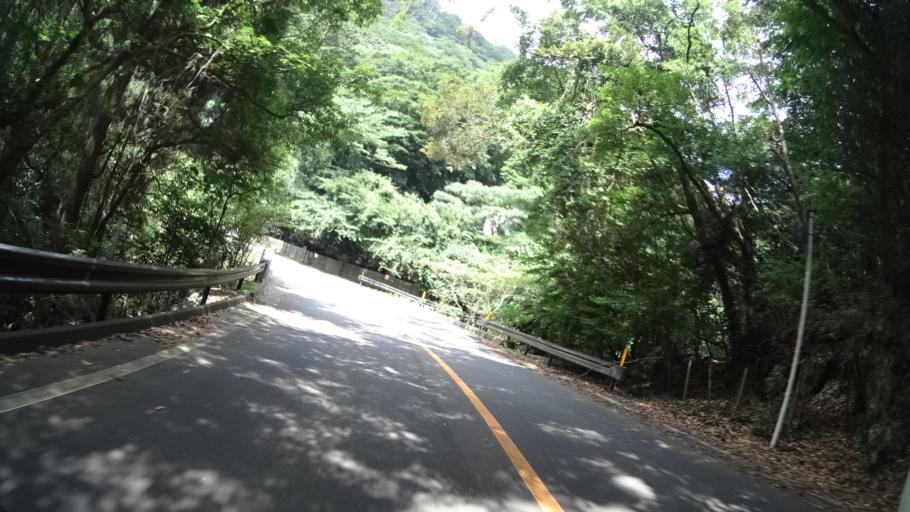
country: JP
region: Miyazaki
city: Kobayashi
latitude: 31.9038
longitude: 130.8401
